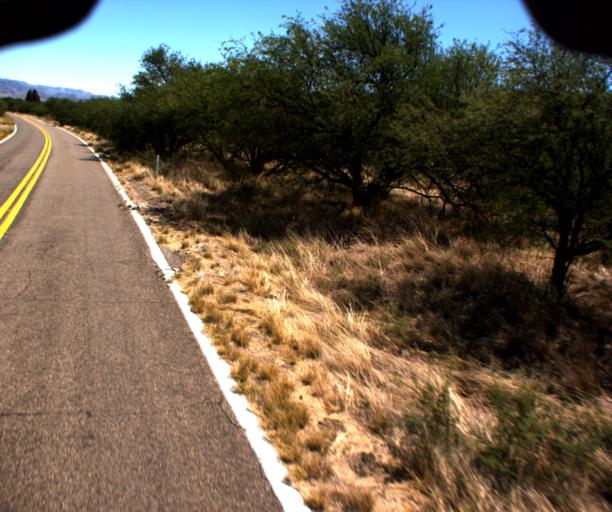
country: US
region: Arizona
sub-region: Santa Cruz County
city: Rio Rico
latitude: 31.4217
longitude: -111.0129
